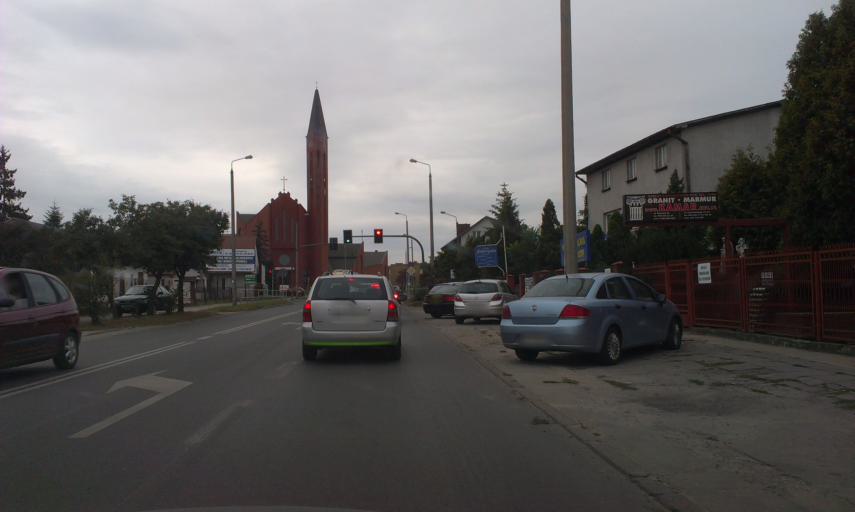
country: PL
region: Masovian Voivodeship
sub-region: Radom
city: Radom
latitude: 51.4106
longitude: 21.1350
